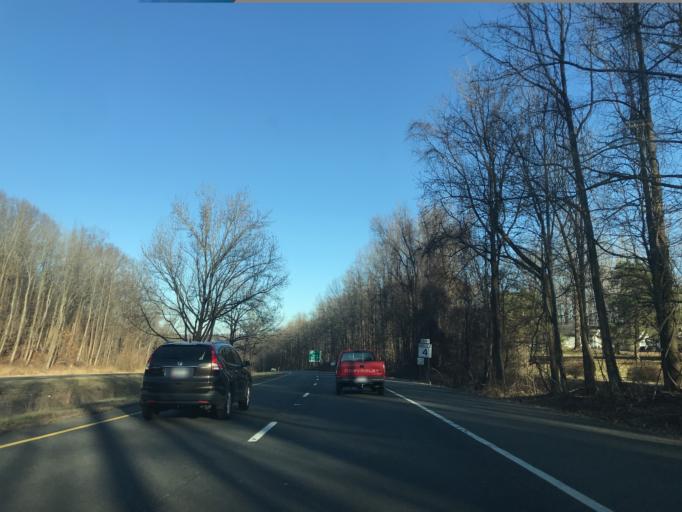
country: US
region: Maryland
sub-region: Prince George's County
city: Upper Marlboro
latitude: 38.8094
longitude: -76.7587
